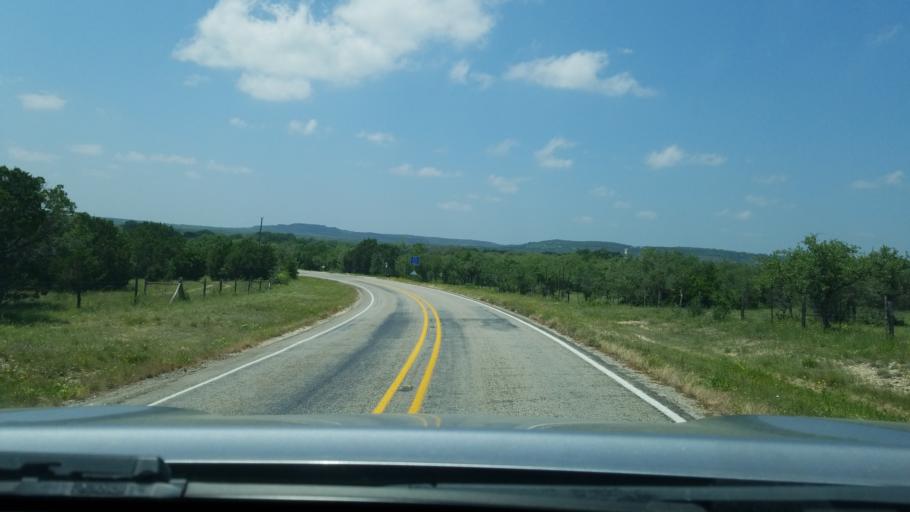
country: US
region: Texas
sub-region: Hays County
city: Woodcreek
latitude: 30.0973
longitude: -98.2385
